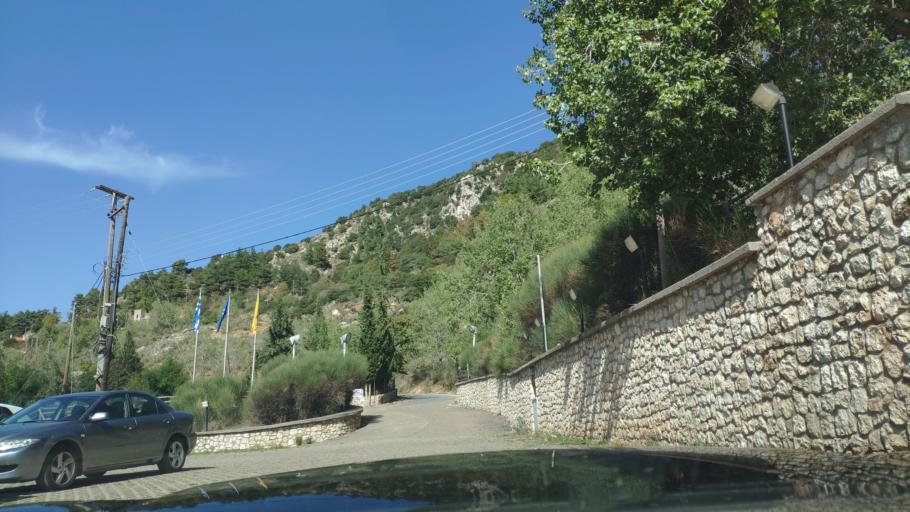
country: GR
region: Peloponnese
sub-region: Nomos Arkadias
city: Dimitsana
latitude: 37.5848
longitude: 22.0467
